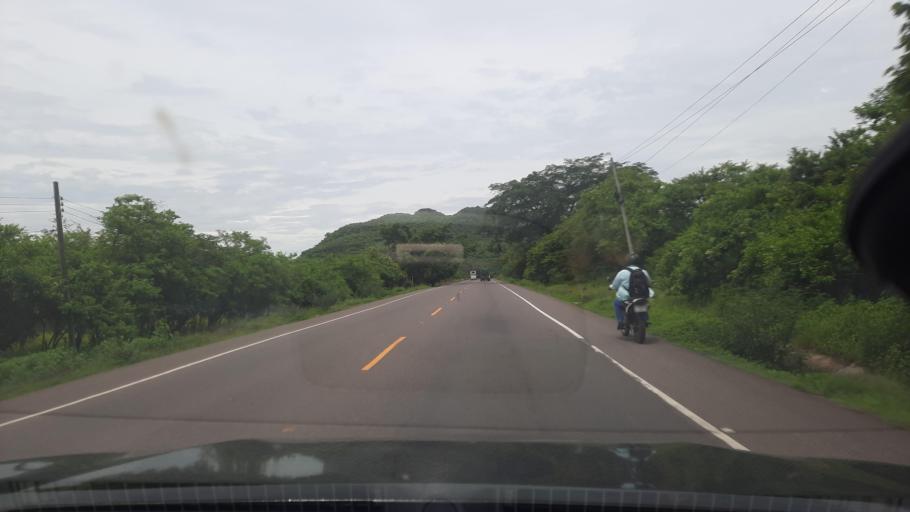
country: HN
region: Valle
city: Langue
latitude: 13.5948
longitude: -87.7032
